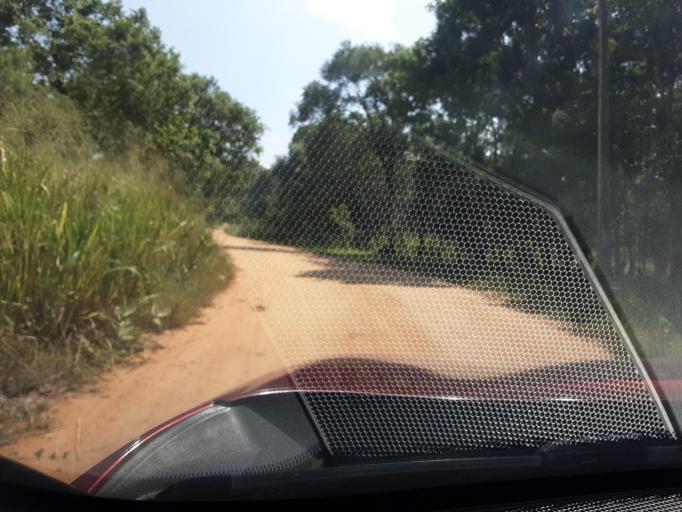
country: LK
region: Central
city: Sigiriya
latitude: 8.0032
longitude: 80.7471
